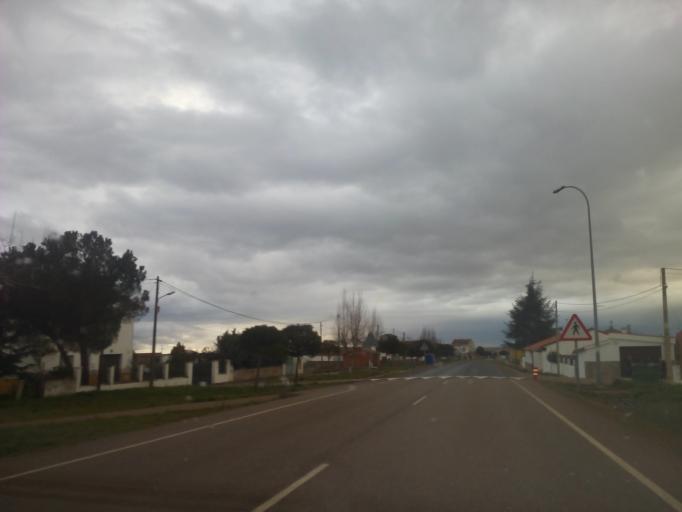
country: ES
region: Castille and Leon
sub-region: Provincia de Salamanca
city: Abusejo
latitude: 40.7070
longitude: -6.1408
